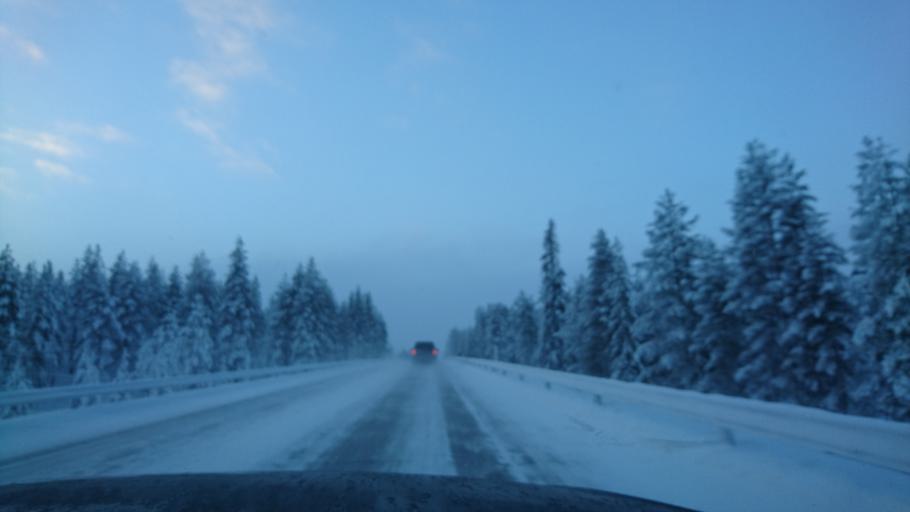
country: FI
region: Northern Ostrobothnia
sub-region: Koillismaa
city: Taivalkoski
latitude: 65.4726
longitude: 27.7389
